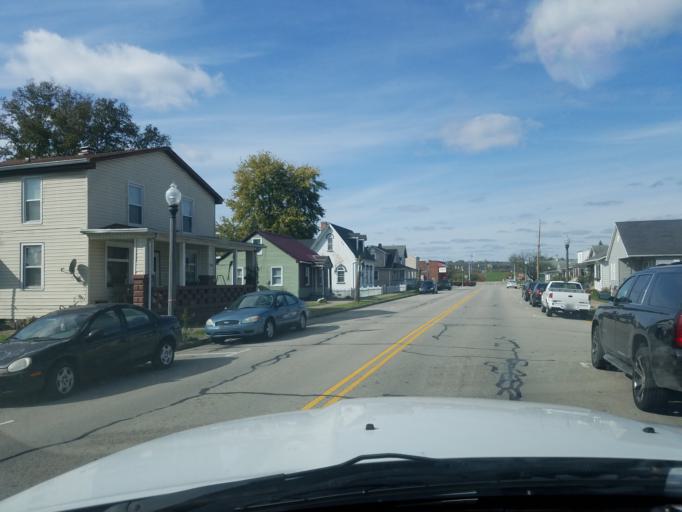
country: US
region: Indiana
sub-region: Dearborn County
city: Lawrenceburg
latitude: 39.0984
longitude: -84.8497
